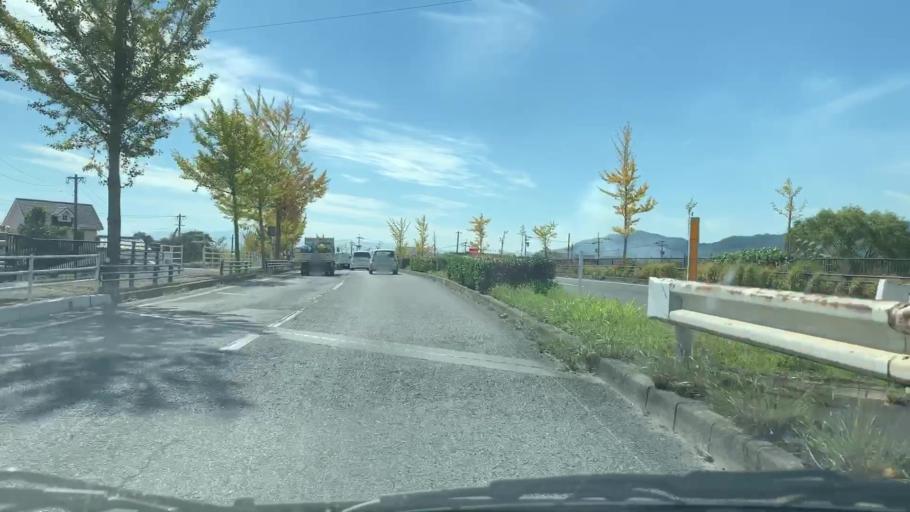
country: JP
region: Saga Prefecture
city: Saga-shi
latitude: 33.2558
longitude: 130.2000
